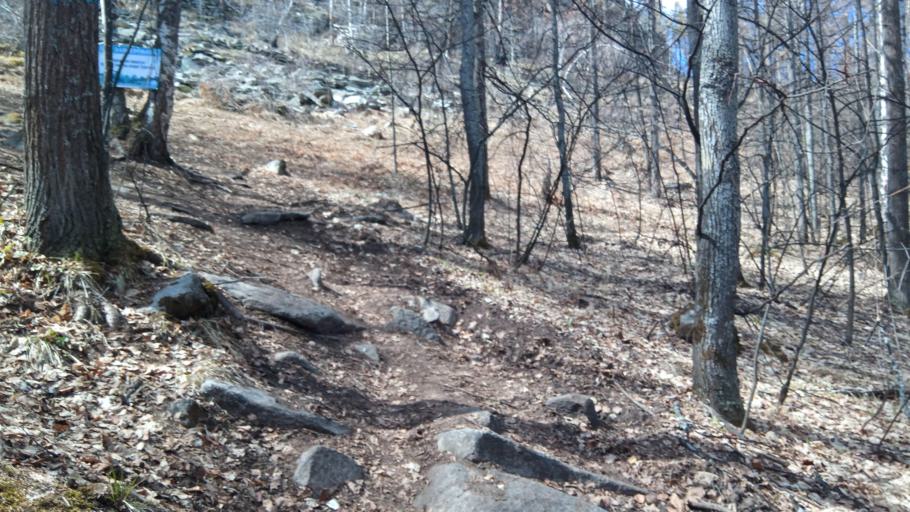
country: RU
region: Chelyabinsk
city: Syrostan
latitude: 55.1665
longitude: 59.9774
